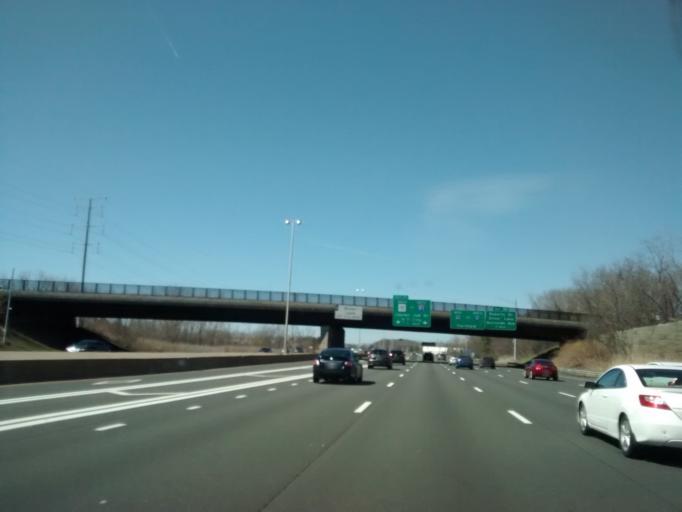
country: US
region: Connecticut
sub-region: Hartford County
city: East Hartford
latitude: 41.7717
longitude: -72.6008
